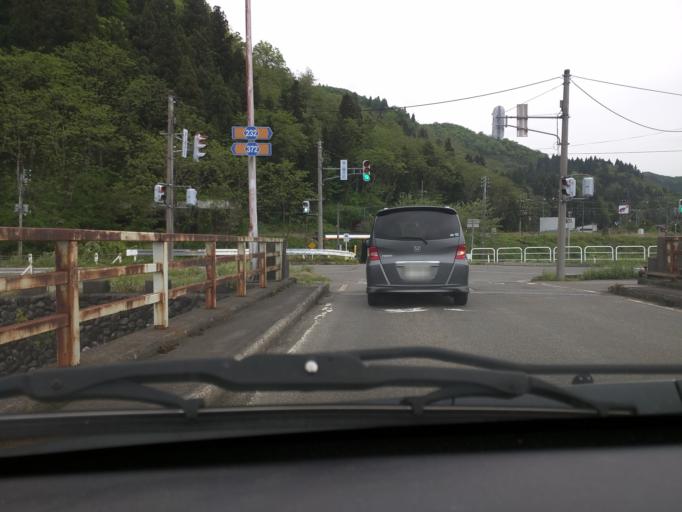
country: JP
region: Niigata
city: Muikamachi
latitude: 37.2074
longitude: 138.9520
